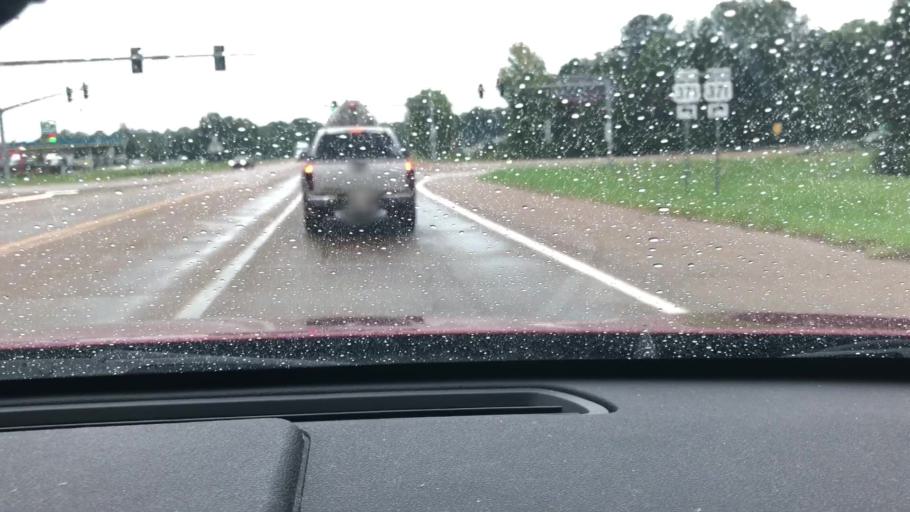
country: US
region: Arkansas
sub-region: Columbia County
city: Magnolia
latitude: 33.2966
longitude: -93.2495
